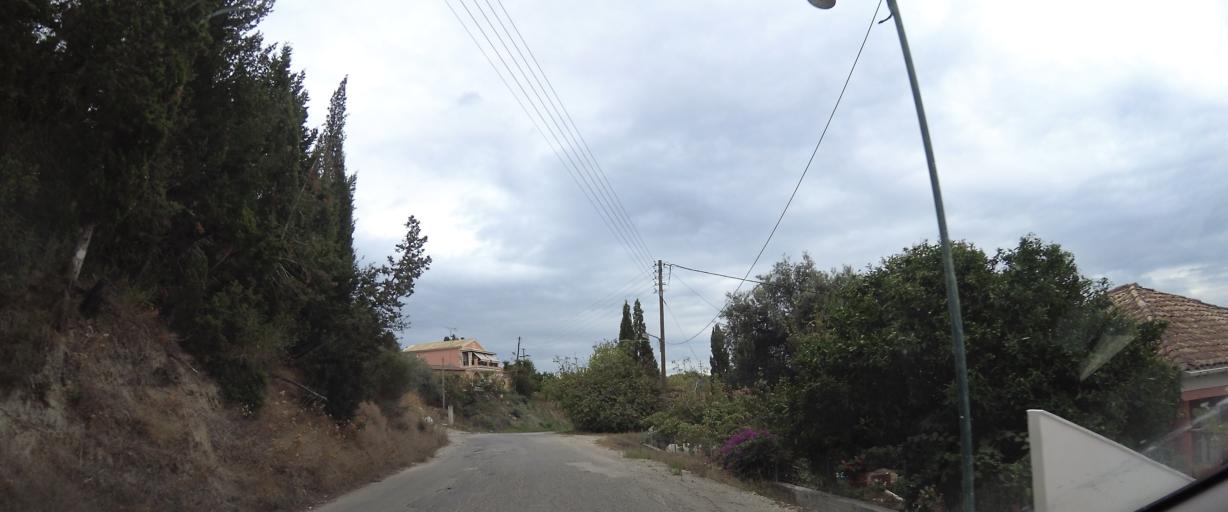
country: GR
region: Ionian Islands
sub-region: Nomos Kerkyras
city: Agios Georgis
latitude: 39.7411
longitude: 19.6771
